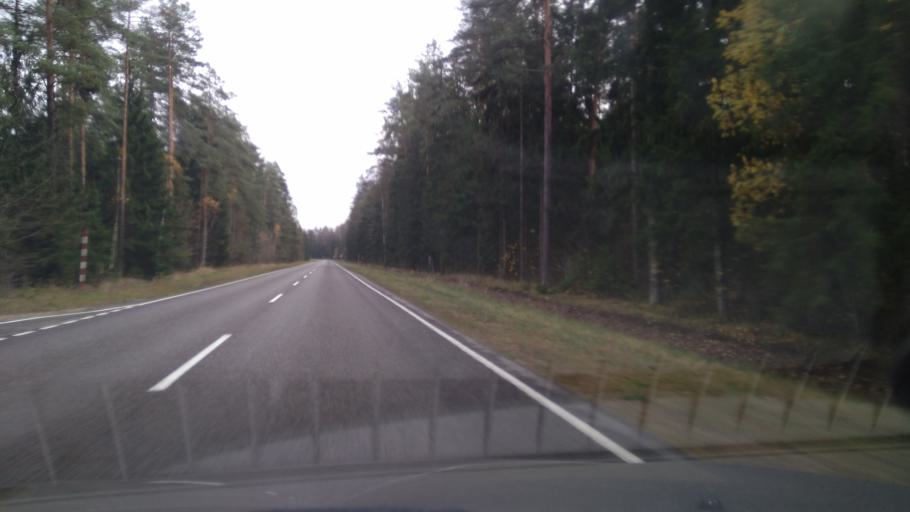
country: BY
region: Minsk
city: Urechcha
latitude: 53.2061
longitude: 27.7928
